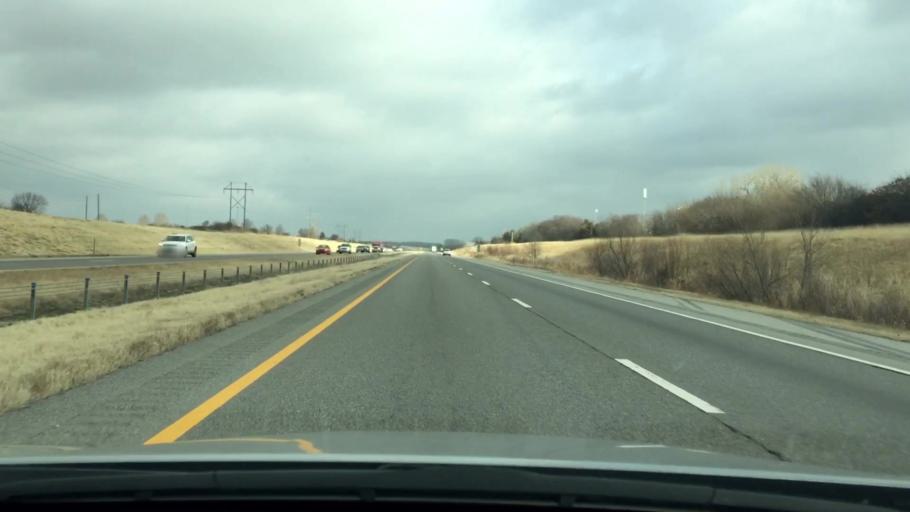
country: US
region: Oklahoma
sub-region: McClain County
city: Purcell
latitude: 35.0200
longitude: -97.3758
